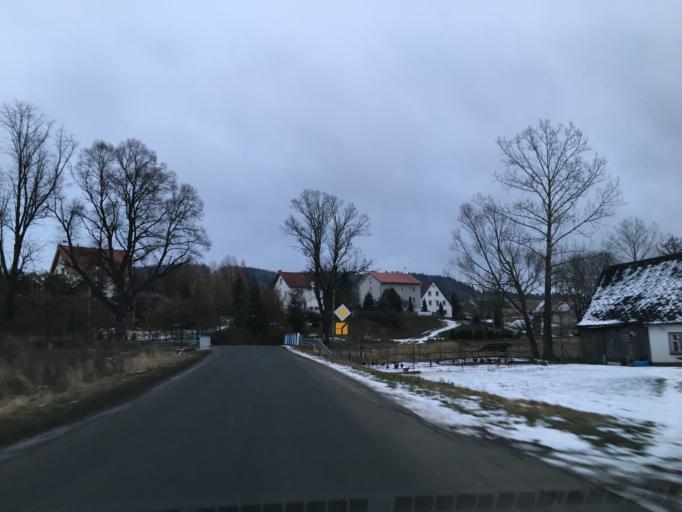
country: PL
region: Lower Silesian Voivodeship
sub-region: Powiat kamiennogorski
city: Krzeszow
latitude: 50.7313
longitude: 16.0731
